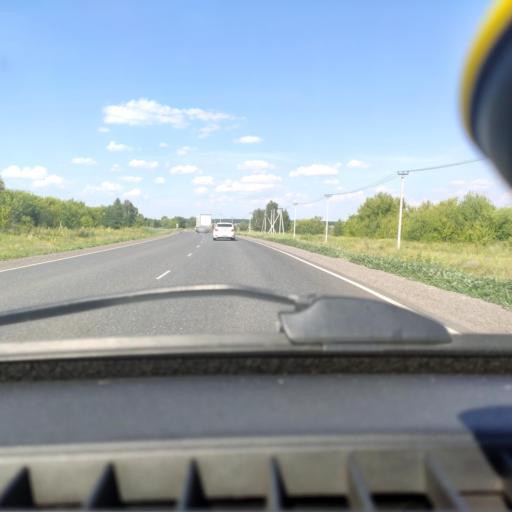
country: RU
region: Samara
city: Povolzhskiy
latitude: 53.6955
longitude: 49.7401
